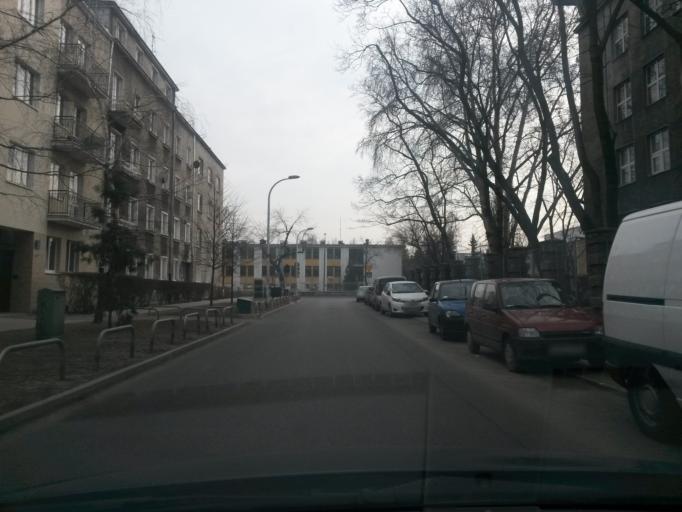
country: PL
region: Masovian Voivodeship
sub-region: Warszawa
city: Mokotow
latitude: 52.2029
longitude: 21.0428
